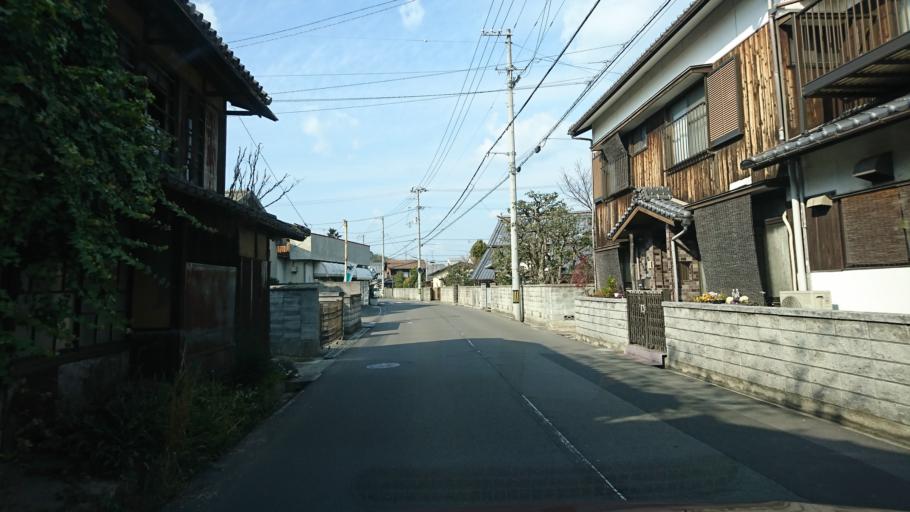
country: JP
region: Ehime
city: Saijo
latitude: 34.0202
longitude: 133.0406
